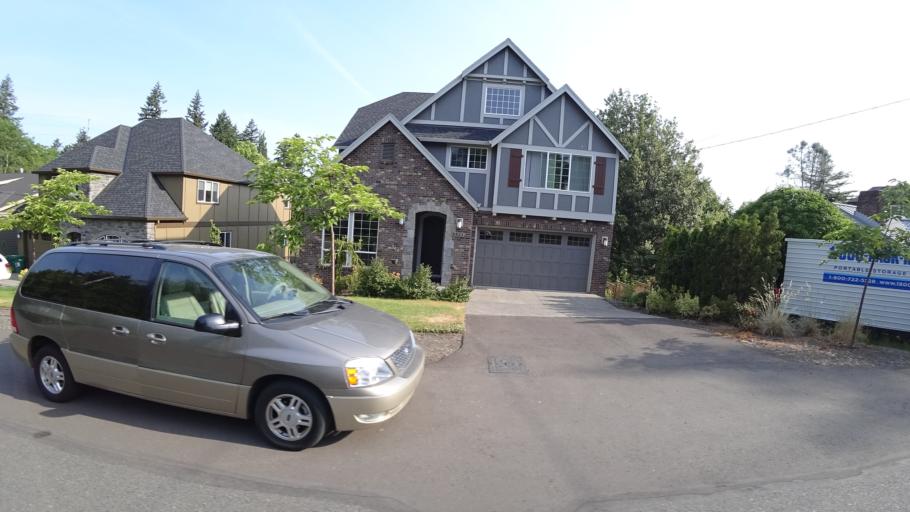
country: US
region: Oregon
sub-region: Washington County
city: Garden Home-Whitford
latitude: 45.4618
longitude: -122.7174
